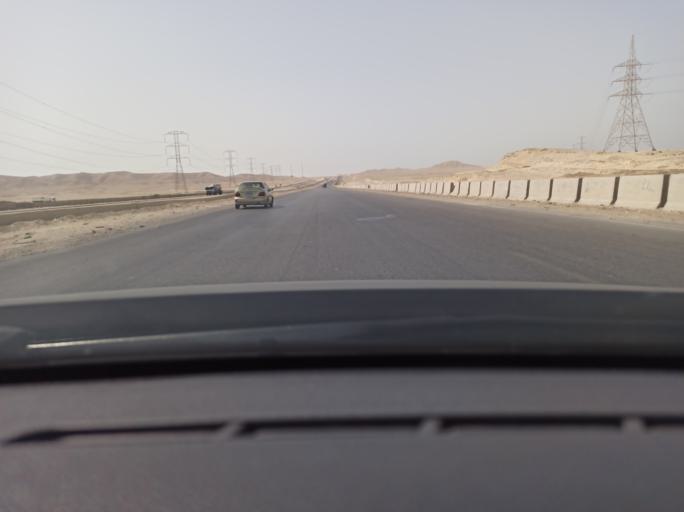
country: EG
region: Al Jizah
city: As Saff
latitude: 29.5583
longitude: 31.4007
